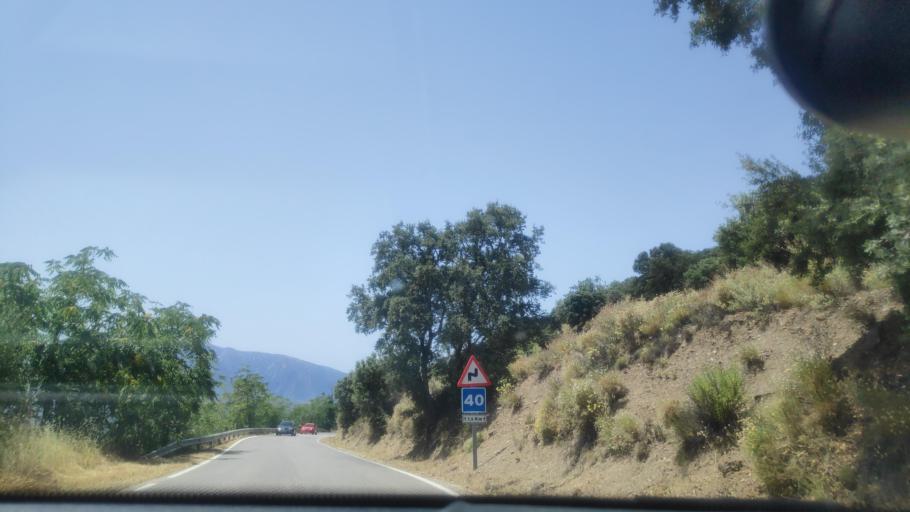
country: ES
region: Andalusia
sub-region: Provincia de Granada
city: Pampaneira
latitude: 36.9300
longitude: -3.3450
